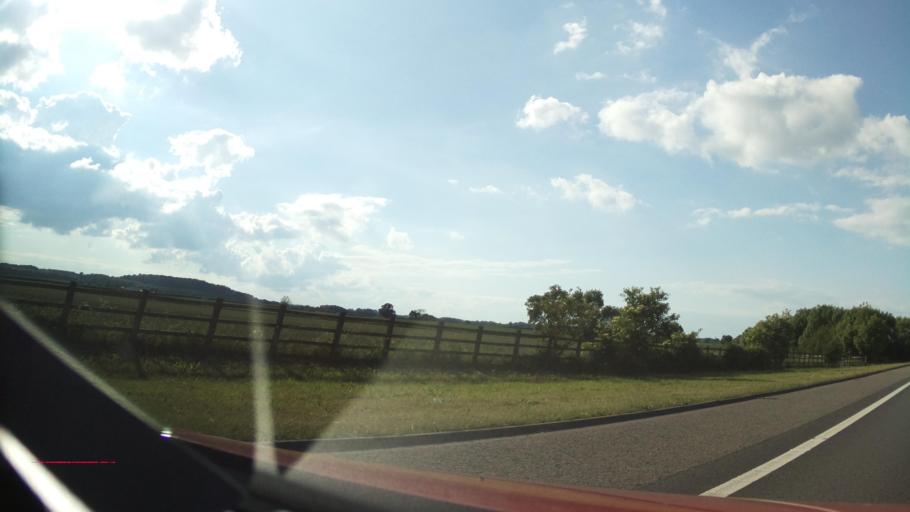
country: GB
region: England
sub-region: Cambridgeshire
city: Sawtry
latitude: 52.4482
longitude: -0.2789
